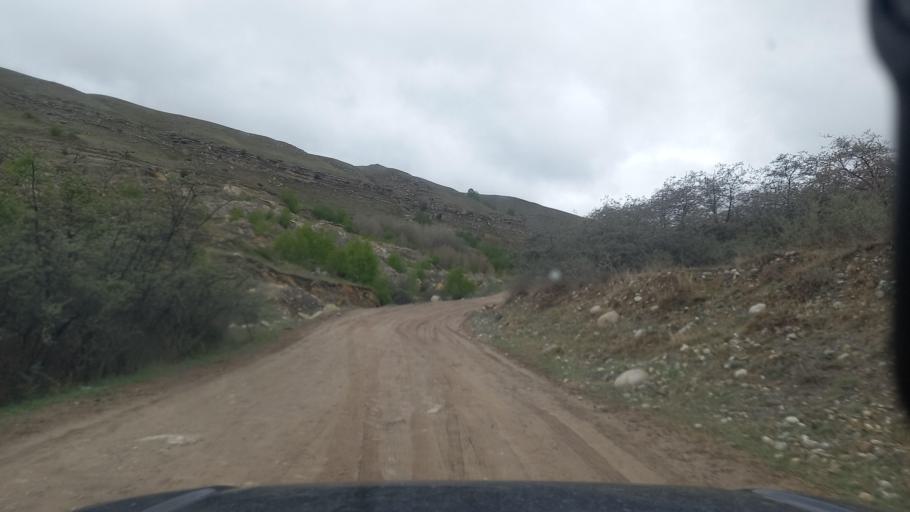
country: RU
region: Kabardino-Balkariya
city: Bylym
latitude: 43.4584
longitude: 42.9969
